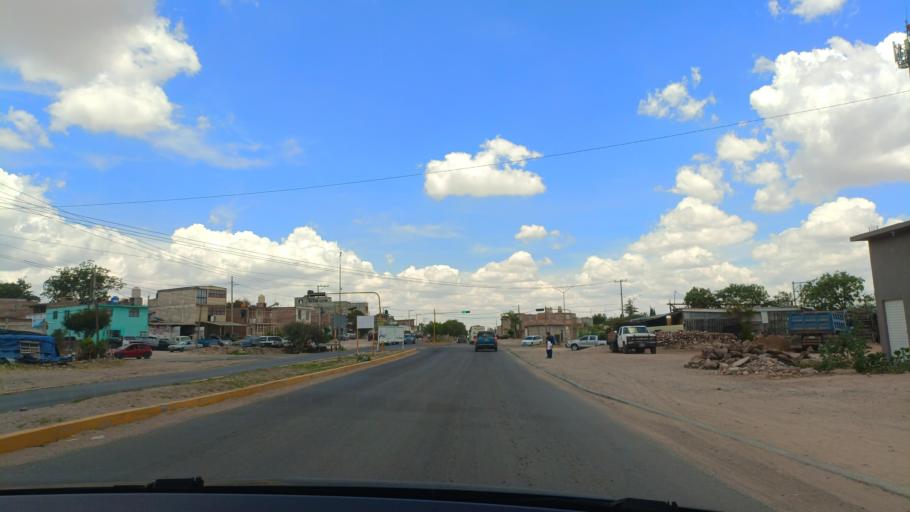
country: MX
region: Guerrero
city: San Luis de la Paz
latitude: 21.2893
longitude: -100.5048
